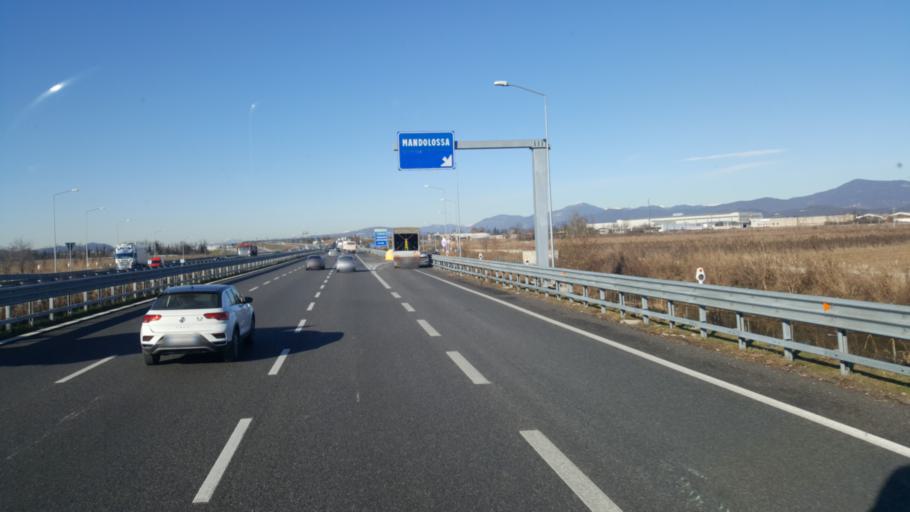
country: IT
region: Lombardy
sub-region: Provincia di Brescia
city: Roncadelle
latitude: 45.5436
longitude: 10.1410
